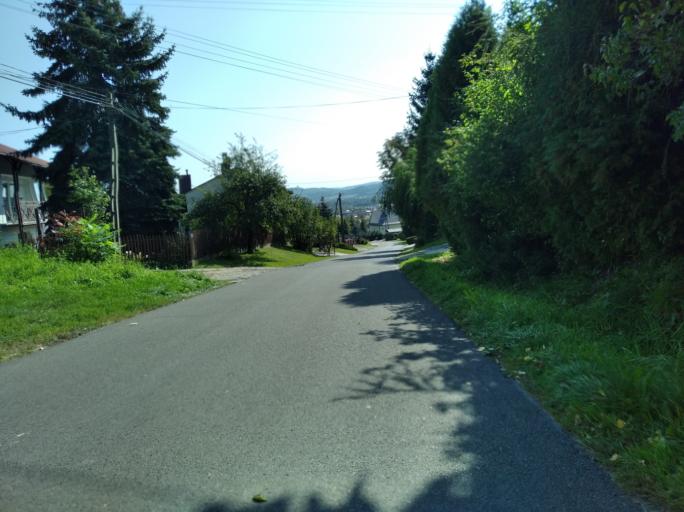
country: PL
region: Subcarpathian Voivodeship
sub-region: Powiat strzyzowski
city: Czudec
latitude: 49.9498
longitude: 21.8346
